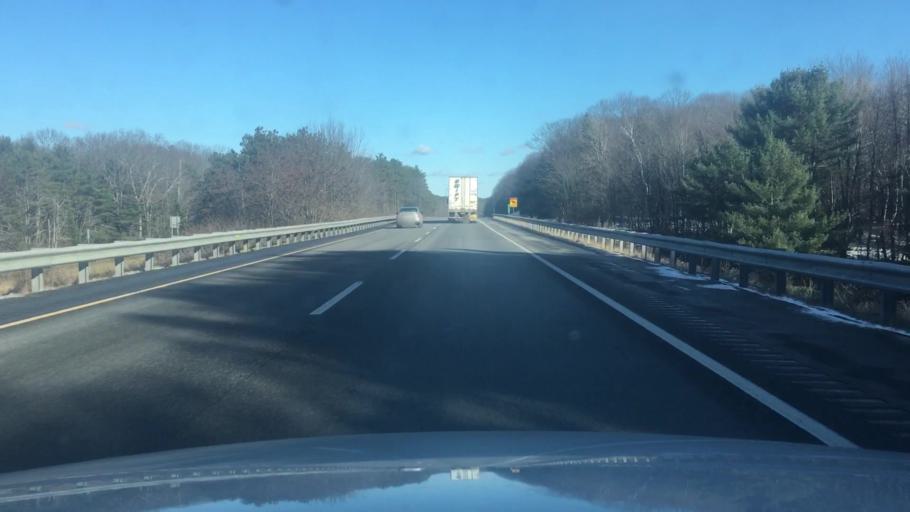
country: US
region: Maine
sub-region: Kennebec County
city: Augusta
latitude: 44.3678
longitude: -69.7751
